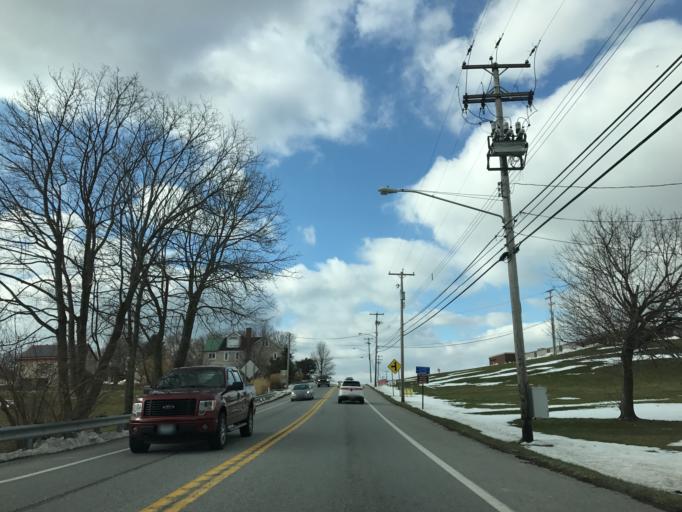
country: US
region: Pennsylvania
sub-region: York County
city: Parkville
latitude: 39.7463
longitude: -76.9476
